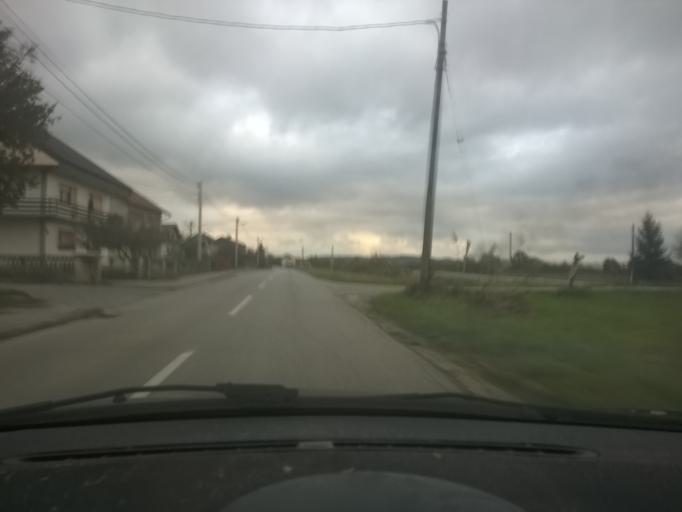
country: HR
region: Zagrebacka
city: Jakovlje
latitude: 45.9885
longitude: 15.8423
